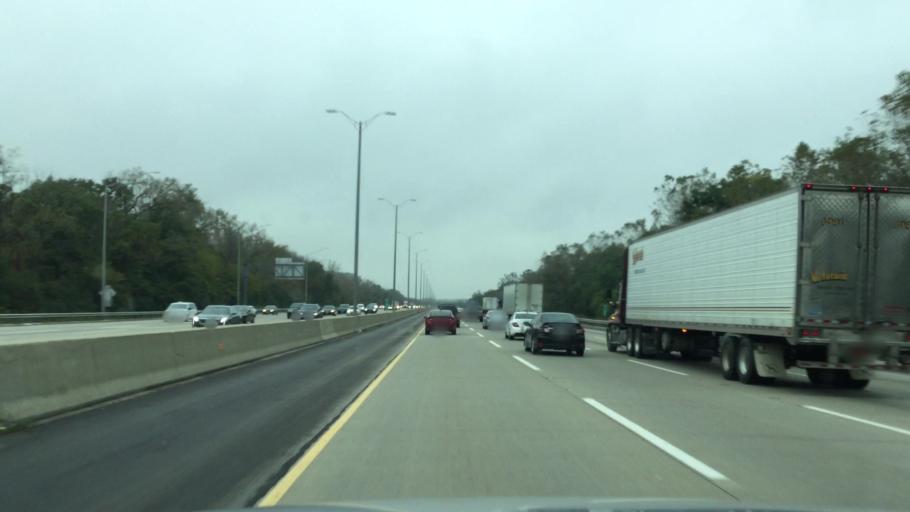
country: US
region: Illinois
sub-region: Lake County
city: Lincolnshire
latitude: 42.2109
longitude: -87.8936
